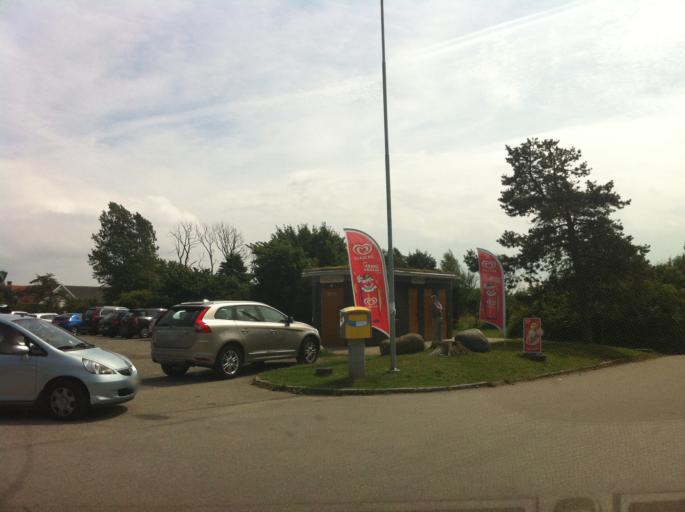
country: SE
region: Skane
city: Smygehamn
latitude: 55.3425
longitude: 13.3306
